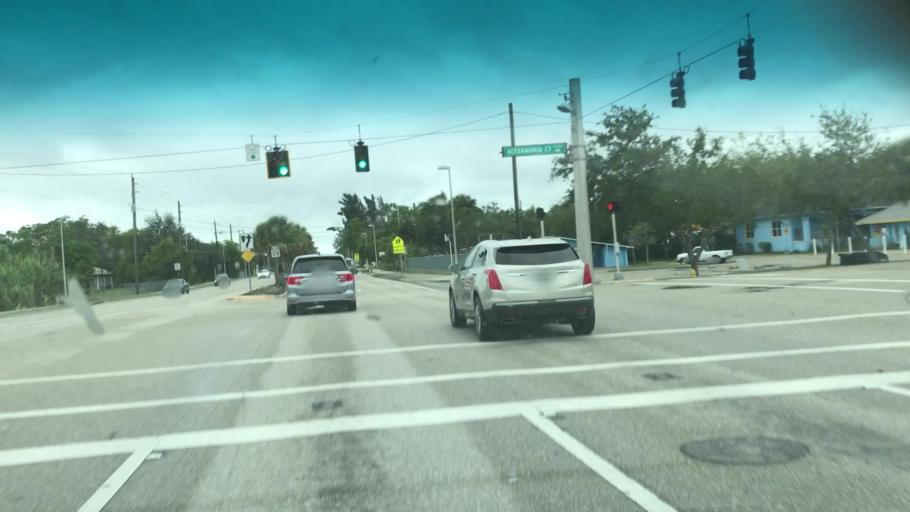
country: US
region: Florida
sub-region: Lee County
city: Harlem Heights
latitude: 26.5183
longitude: -81.9249
